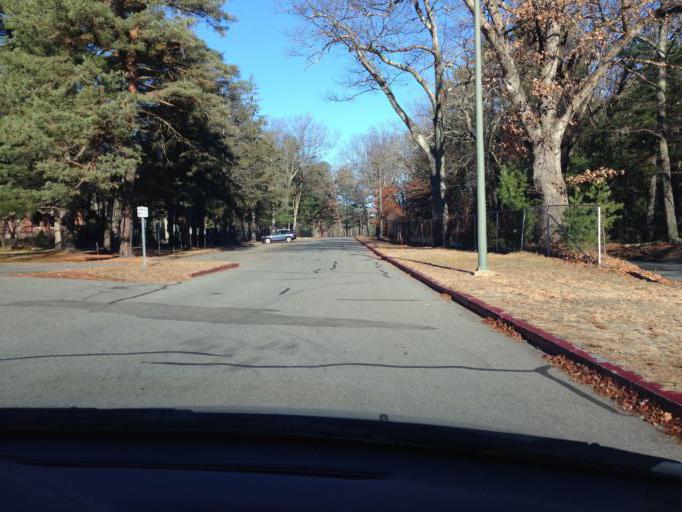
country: US
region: Massachusetts
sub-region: Middlesex County
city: Bedford
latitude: 42.5074
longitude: -71.2736
